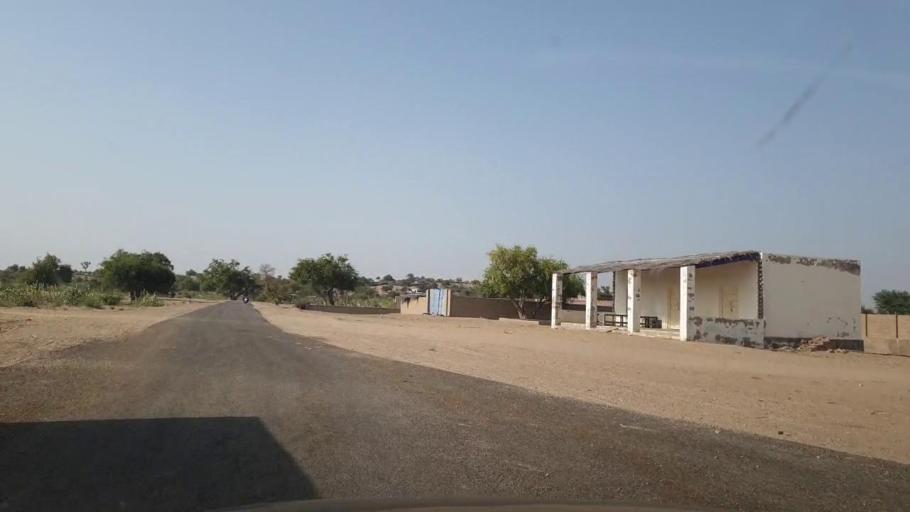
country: PK
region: Sindh
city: Islamkot
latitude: 25.1618
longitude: 70.5226
